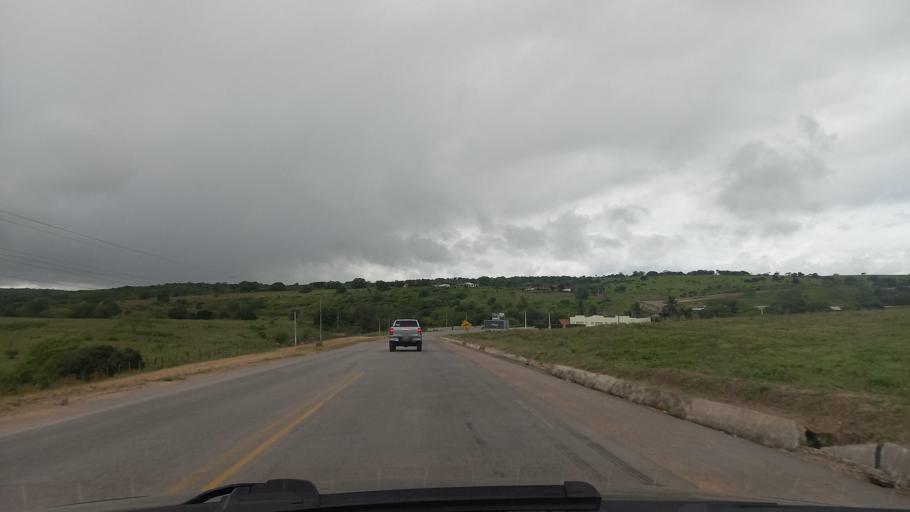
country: BR
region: Alagoas
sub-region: Batalha
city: Batalha
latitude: -9.6316
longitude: -37.2034
